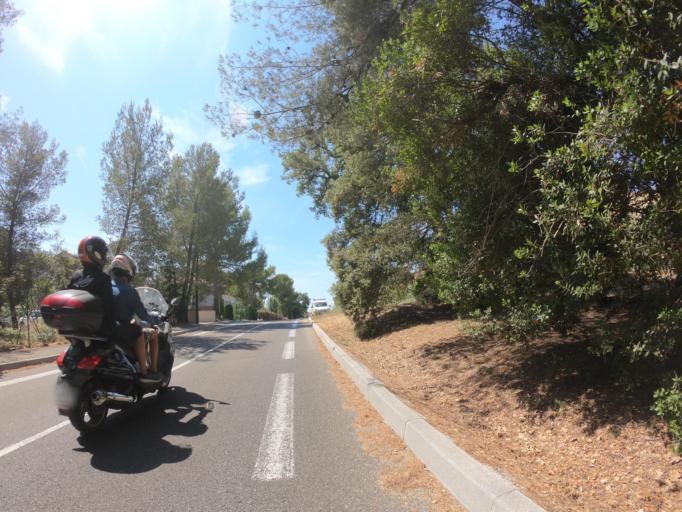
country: FR
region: Provence-Alpes-Cote d'Azur
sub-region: Departement du Var
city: La Garde
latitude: 43.1181
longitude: 5.9990
